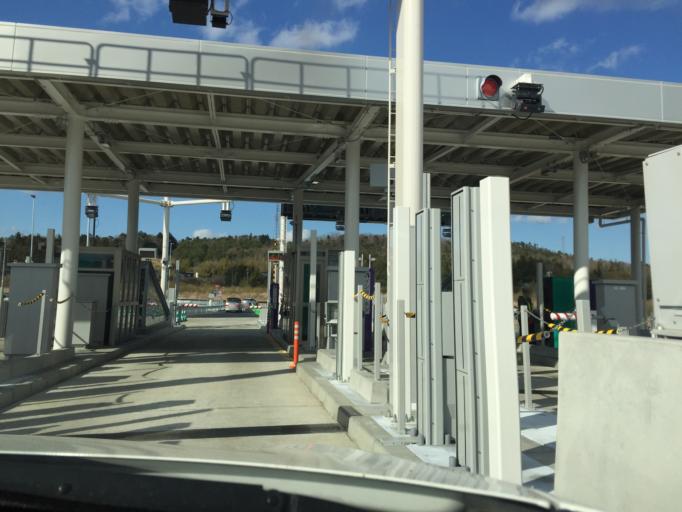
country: JP
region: Fukushima
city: Namie
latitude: 37.4121
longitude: 140.9639
